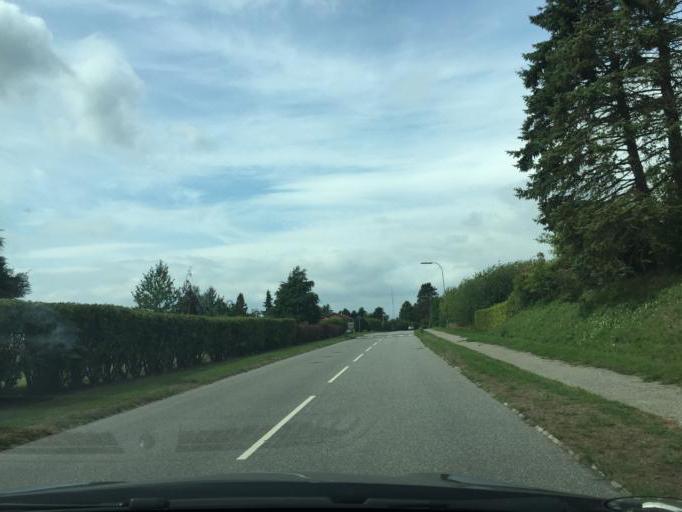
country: DK
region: South Denmark
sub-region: Assens Kommune
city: Tommerup Stationsby
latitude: 55.3891
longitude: 10.1935
